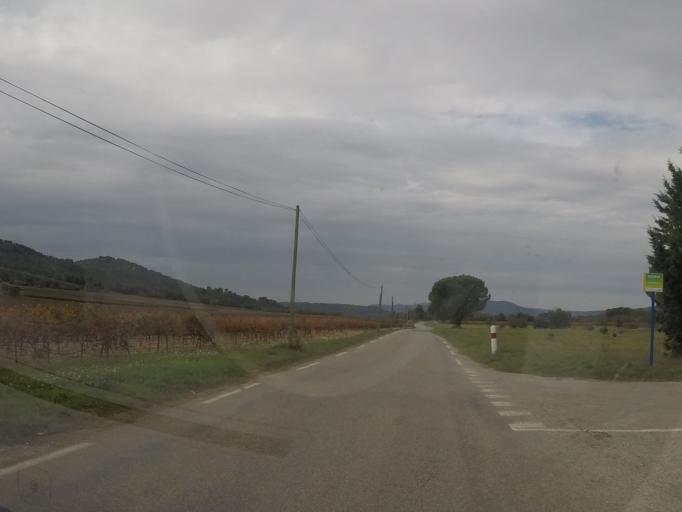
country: FR
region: Provence-Alpes-Cote d'Azur
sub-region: Departement du Vaucluse
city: Villelaure
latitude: 43.7426
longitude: 5.4298
